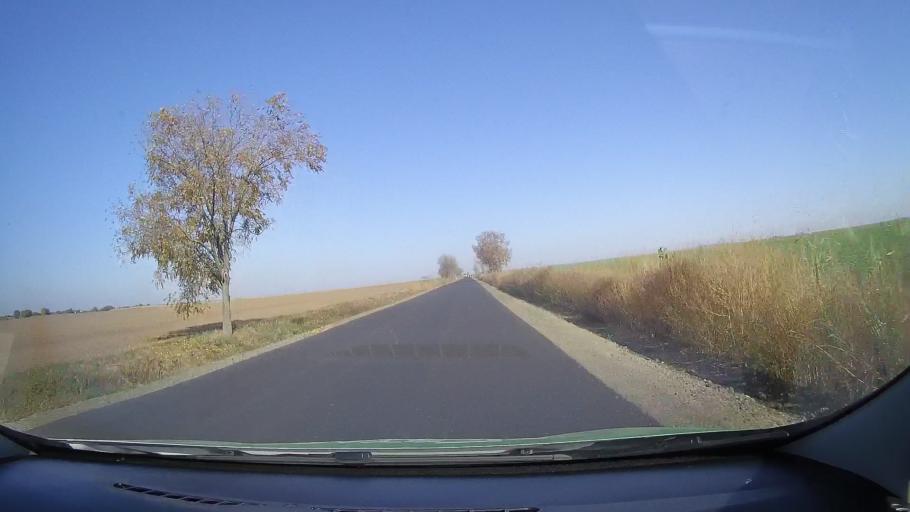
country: RO
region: Satu Mare
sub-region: Comuna Tiream
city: Tiream
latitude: 47.6257
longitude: 22.4678
